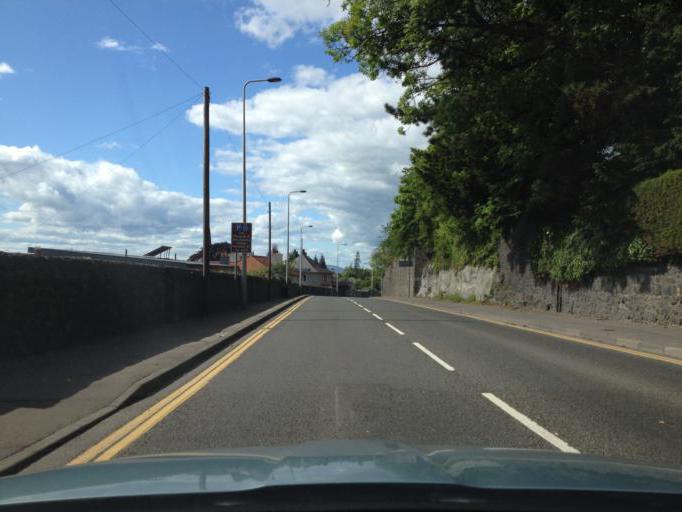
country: GB
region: Scotland
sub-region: Perth and Kinross
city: Perth
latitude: 56.3919
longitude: -3.4194
